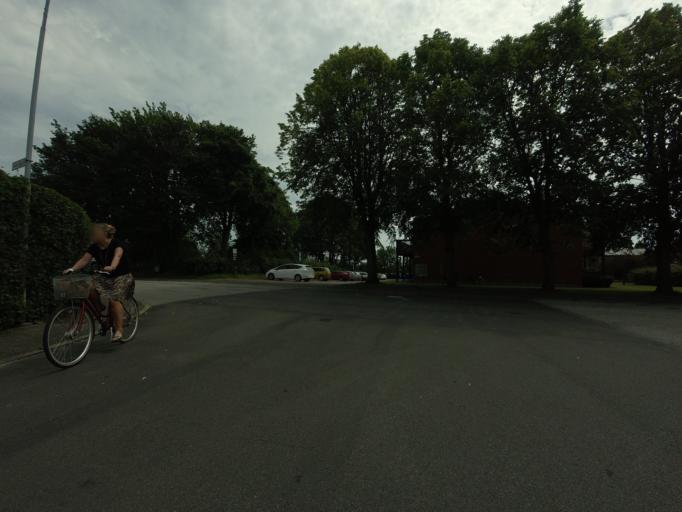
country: SE
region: Skane
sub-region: Ystads Kommun
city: Ystad
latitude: 55.4274
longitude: 13.8041
